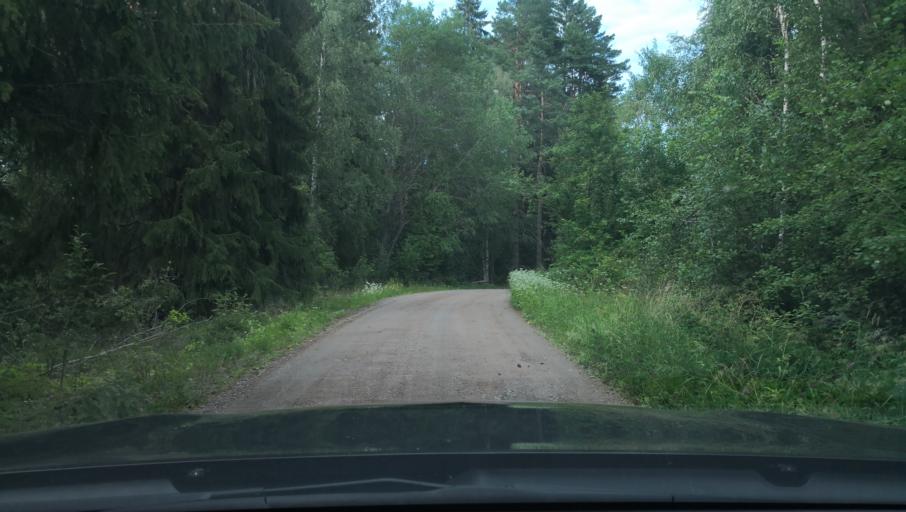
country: SE
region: Vaestmanland
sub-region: Surahammars Kommun
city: Surahammar
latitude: 59.6602
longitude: 16.1556
